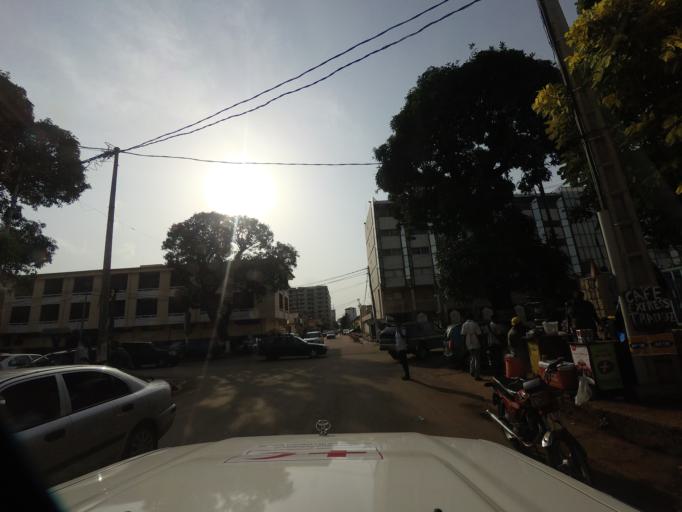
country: GN
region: Conakry
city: Camayenne
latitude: 9.5104
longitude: -13.7151
